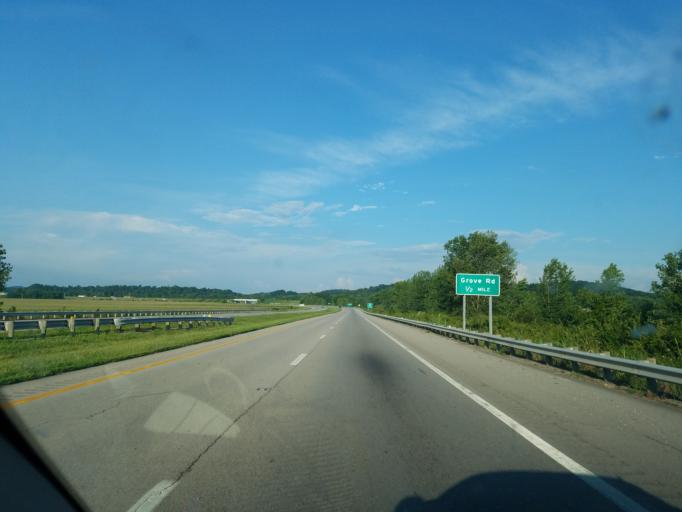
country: US
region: Ohio
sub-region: Pike County
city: Piketon
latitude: 39.0462
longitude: -83.0375
